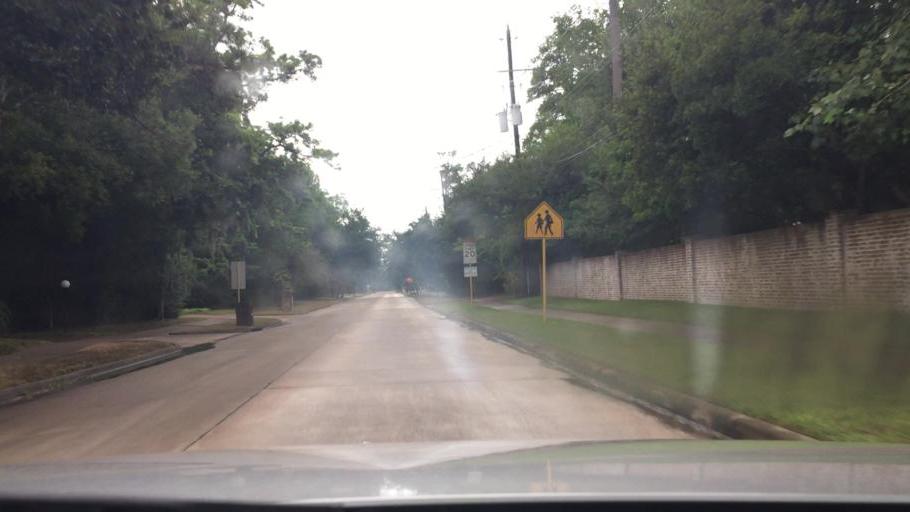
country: US
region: Texas
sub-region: Harris County
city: Hedwig Village
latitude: 29.7711
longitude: -95.5176
